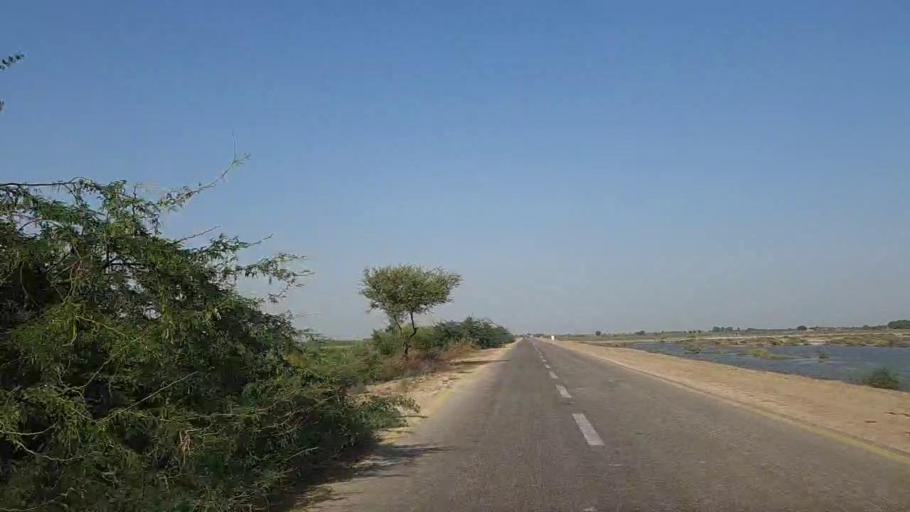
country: PK
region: Sindh
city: Jati
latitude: 24.3979
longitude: 68.2918
